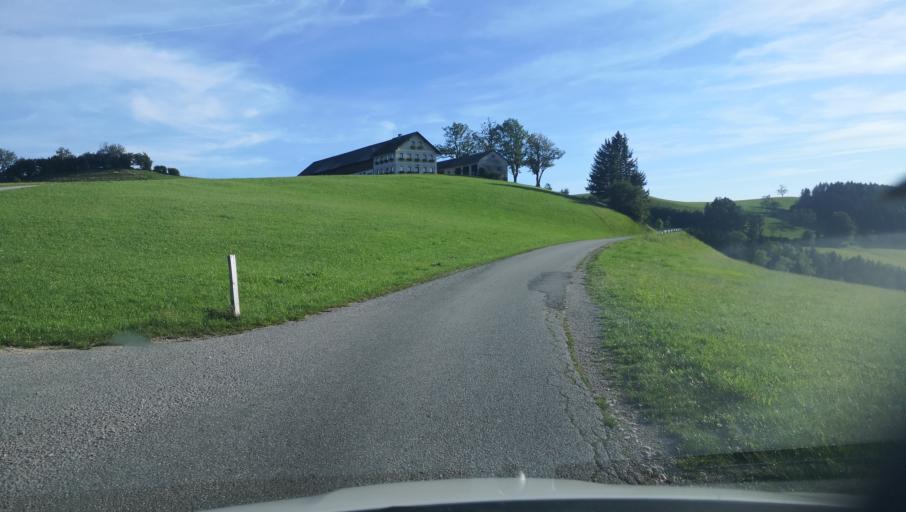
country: AT
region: Lower Austria
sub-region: Politischer Bezirk Amstetten
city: Neuhofen an der Ybbs
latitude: 48.0128
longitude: 14.8916
